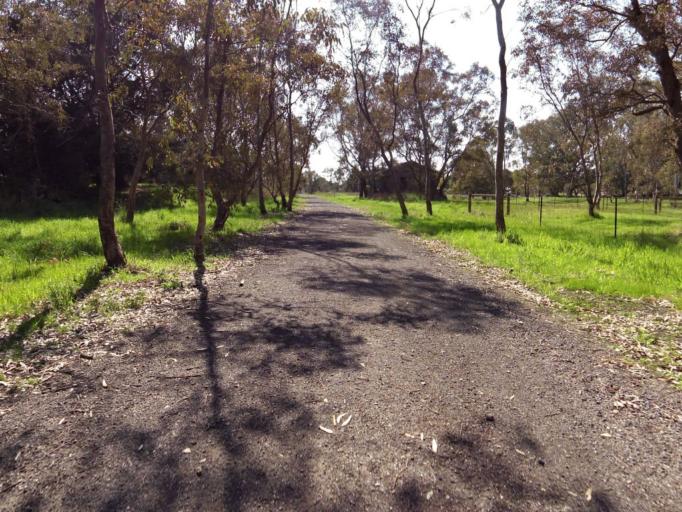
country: AU
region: Victoria
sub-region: Murrindindi
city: Alexandra
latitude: -37.1053
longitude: 145.6161
